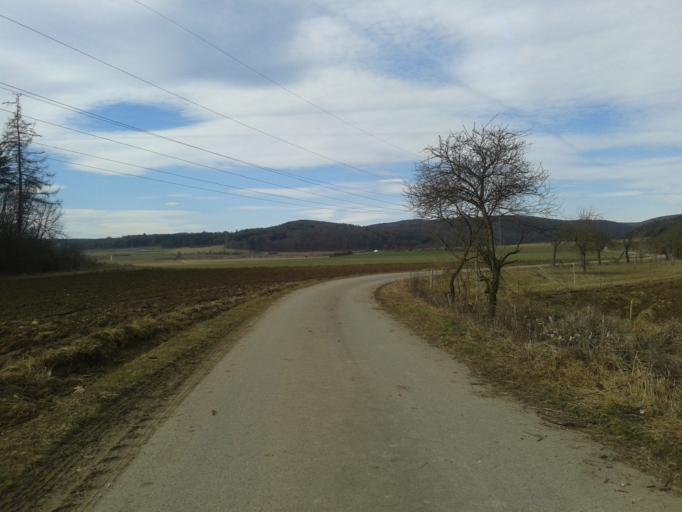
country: DE
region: Baden-Wuerttemberg
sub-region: Tuebingen Region
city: Altheim
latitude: 48.3498
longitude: 9.7544
